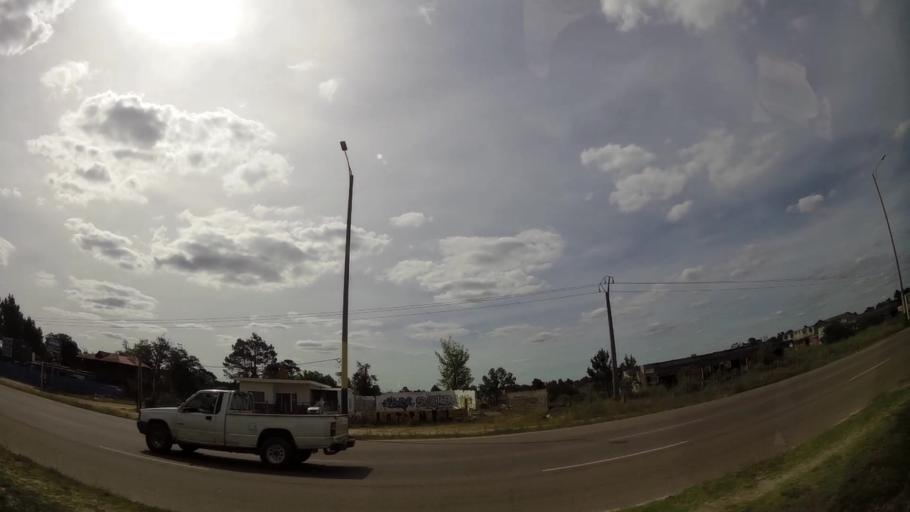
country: UY
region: Canelones
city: Pando
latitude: -34.8066
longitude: -55.9306
